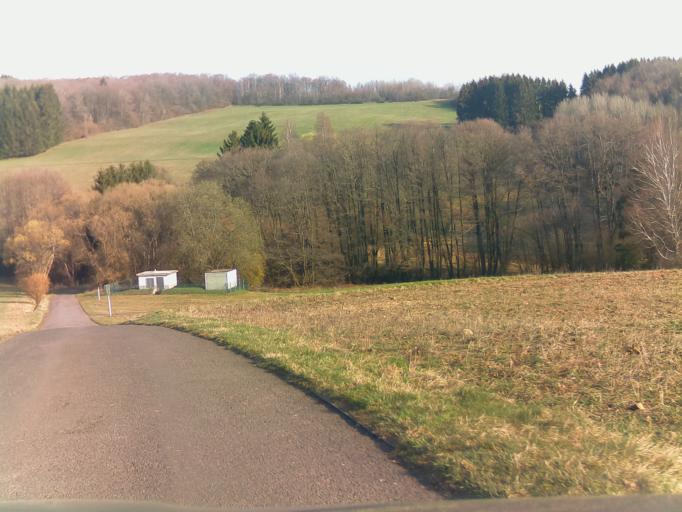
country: DE
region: Rheinland-Pfalz
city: Achtelsbach
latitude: 49.5754
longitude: 7.0541
